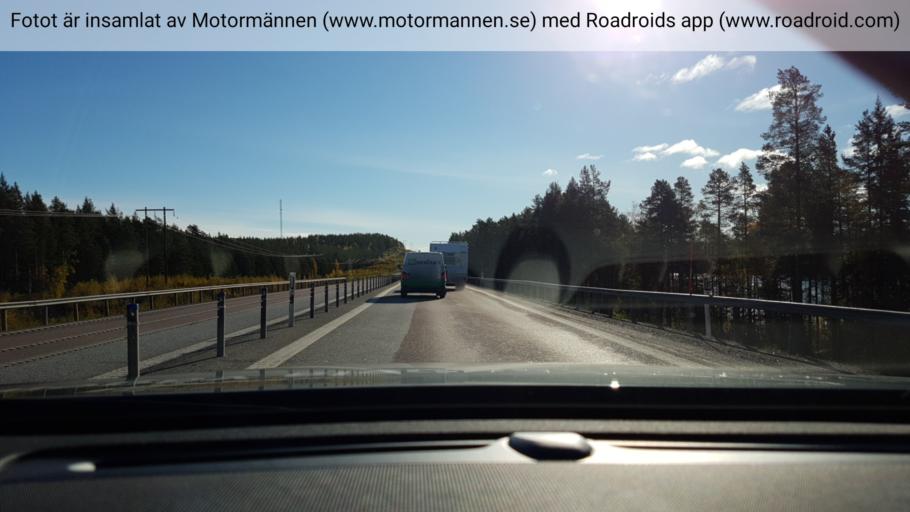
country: SE
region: Vaesterbotten
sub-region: Skelleftea Kommun
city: Soedra Bergsbyn
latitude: 64.6630
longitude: 21.1039
